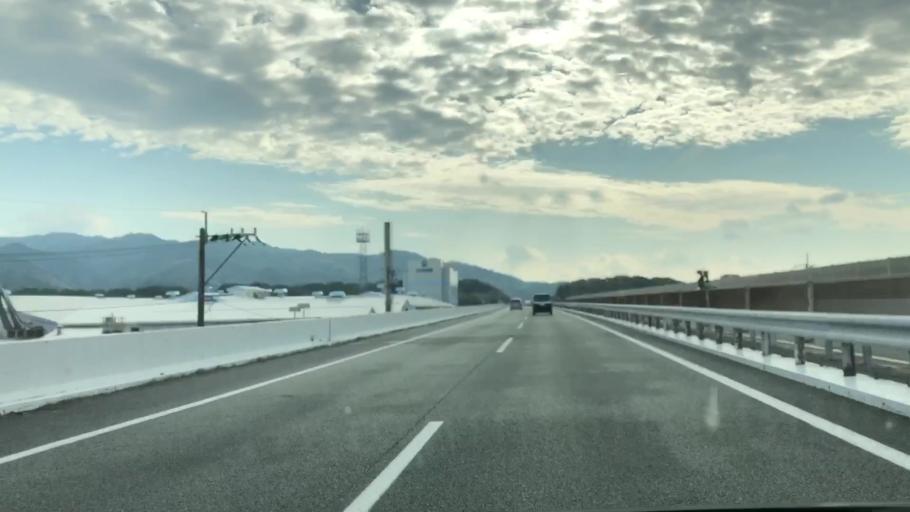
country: JP
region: Fukuoka
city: Setakamachi-takayanagi
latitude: 33.1869
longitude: 130.5192
